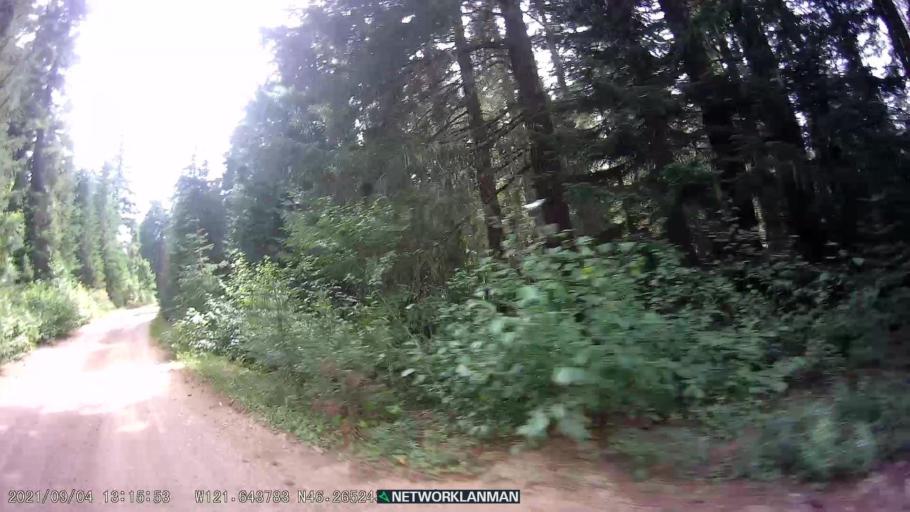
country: US
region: Washington
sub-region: Klickitat County
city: White Salmon
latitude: 46.2652
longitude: -121.6437
